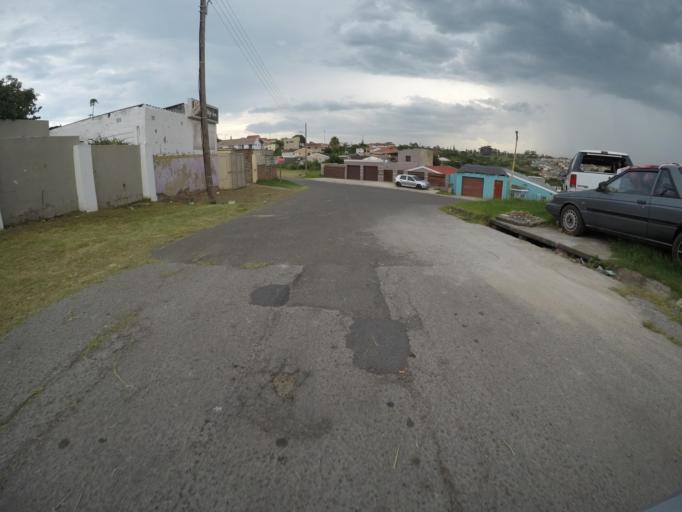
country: ZA
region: Eastern Cape
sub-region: Buffalo City Metropolitan Municipality
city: East London
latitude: -33.0213
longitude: 27.8673
